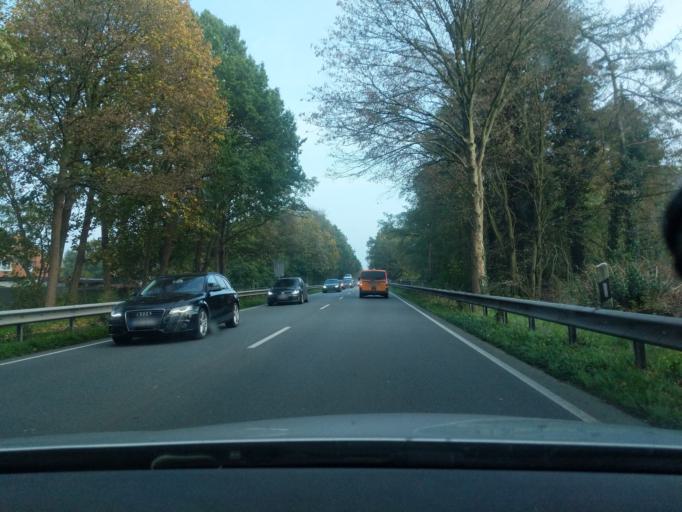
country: DE
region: Lower Saxony
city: Stade
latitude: 53.5830
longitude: 9.4818
